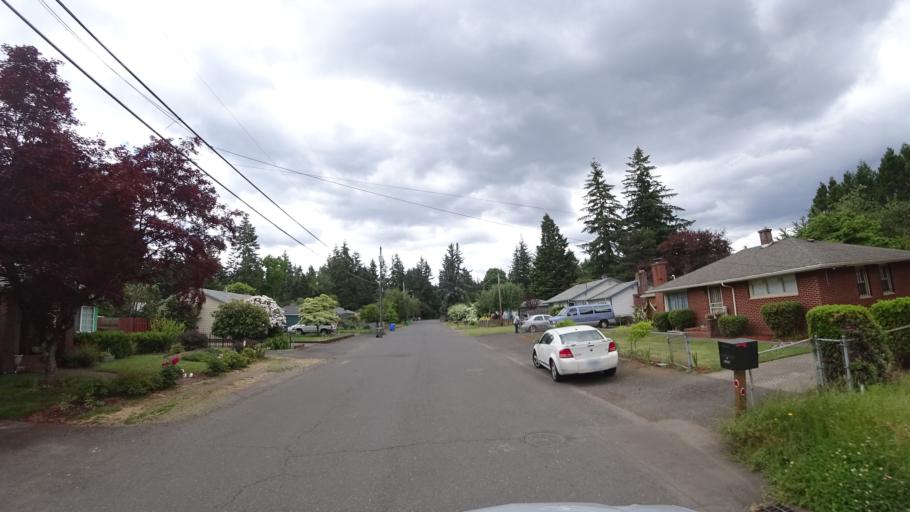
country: US
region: Oregon
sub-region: Clackamas County
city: Happy Valley
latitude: 45.5027
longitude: -122.5060
